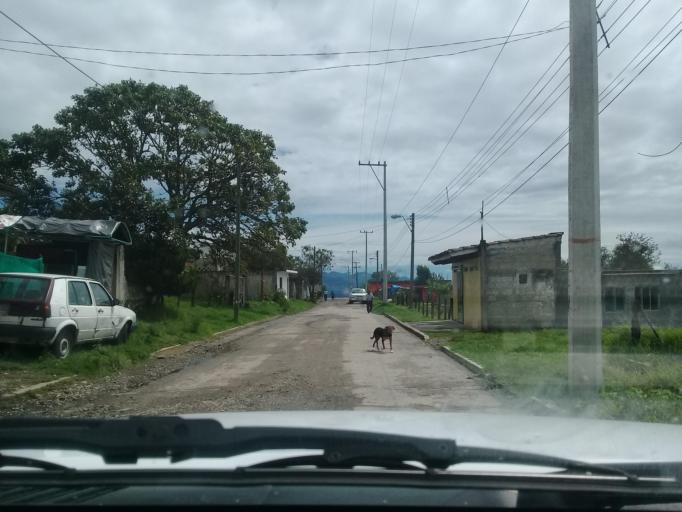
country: MX
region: Veracruz
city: Rafael Lucio
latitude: 19.5930
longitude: -96.9856
